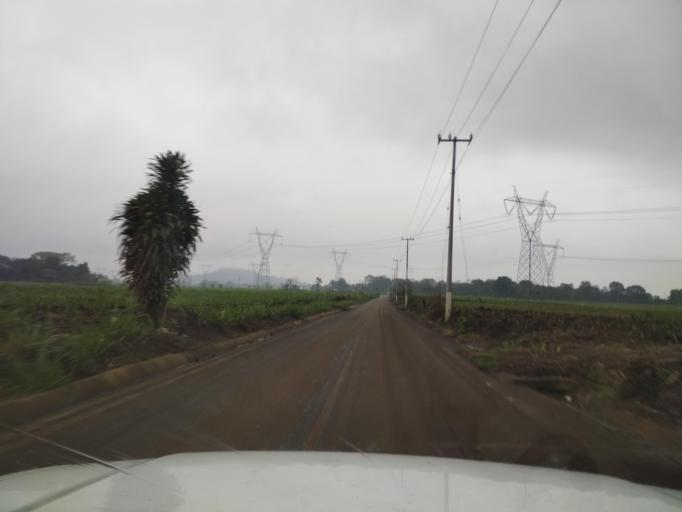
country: MX
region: Veracruz
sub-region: Cordoba
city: Veinte de Noviembre
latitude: 18.8615
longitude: -96.9599
